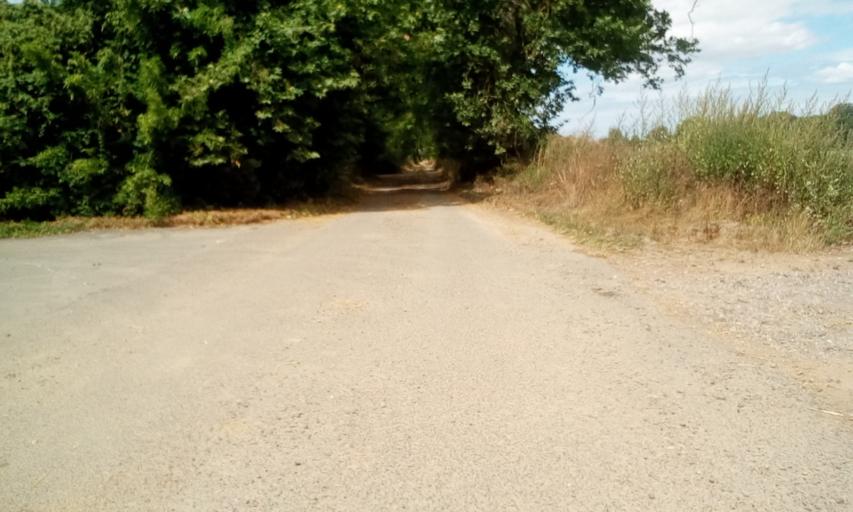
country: FR
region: Lower Normandy
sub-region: Departement du Calvados
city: Bellengreville
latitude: 49.1486
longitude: -0.2080
